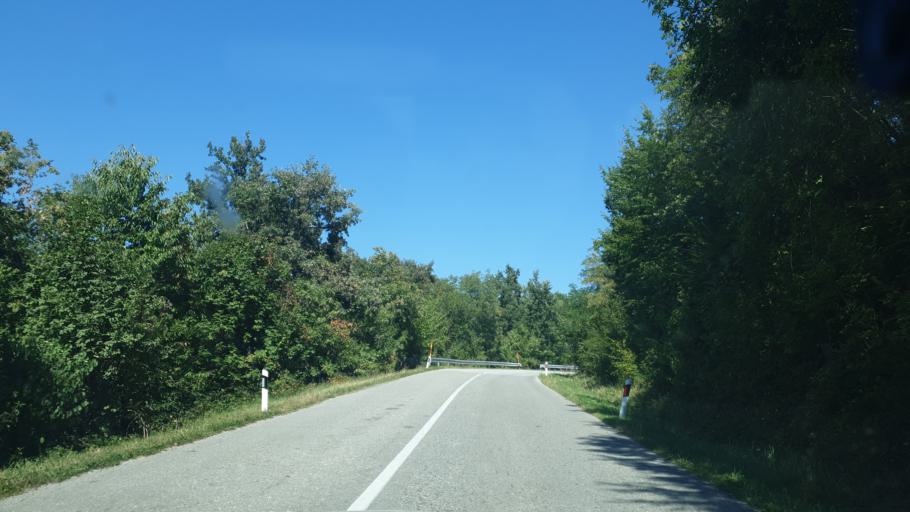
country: RS
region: Central Serbia
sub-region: Kolubarski Okrug
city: Mionica
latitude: 44.1550
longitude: 20.0005
